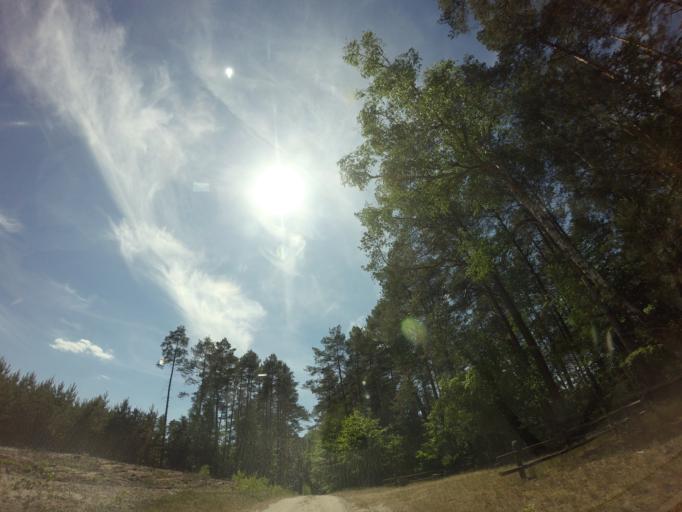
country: PL
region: West Pomeranian Voivodeship
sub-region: Powiat choszczenski
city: Drawno
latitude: 53.1234
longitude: 15.8271
